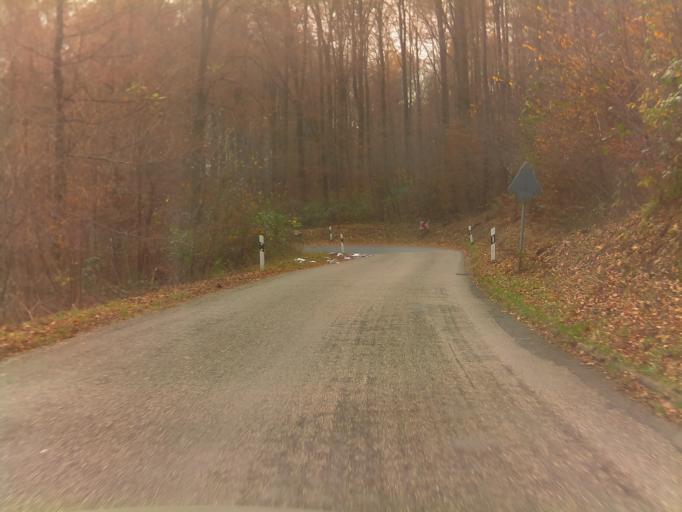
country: DE
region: Baden-Wuerttemberg
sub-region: Karlsruhe Region
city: Gaiberg
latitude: 49.3827
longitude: 8.7598
